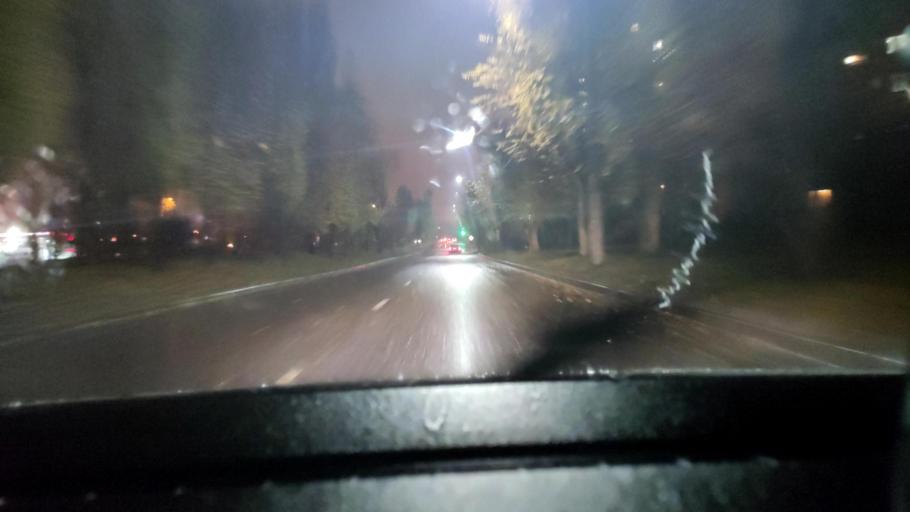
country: RU
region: Voronezj
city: Voronezh
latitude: 51.6569
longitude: 39.1328
